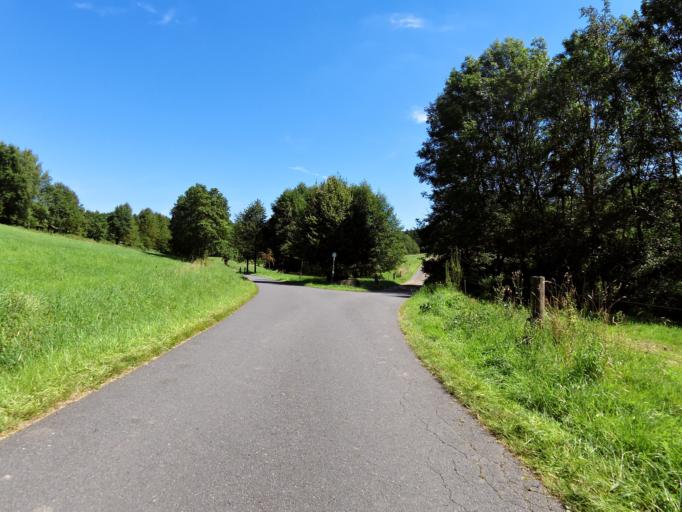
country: DE
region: Hesse
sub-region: Regierungsbezirk Darmstadt
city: Erbach
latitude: 49.6453
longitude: 8.9391
